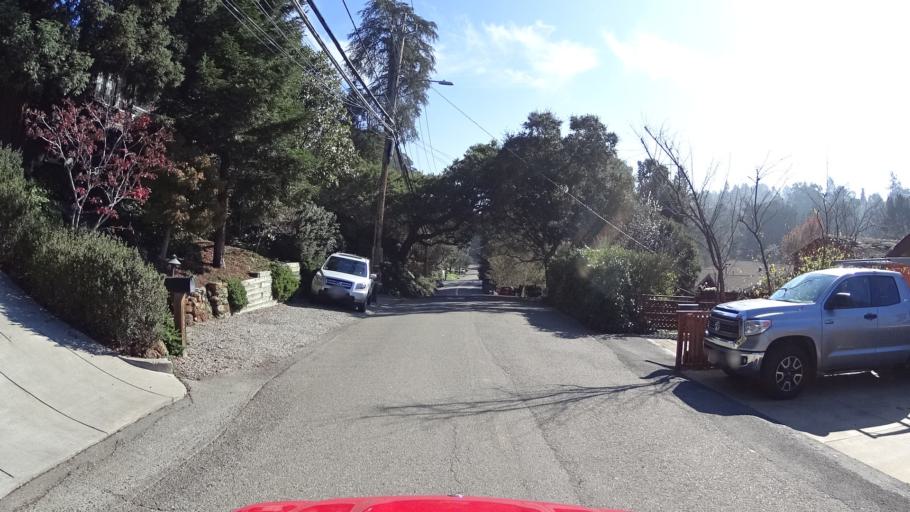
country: US
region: California
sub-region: Alameda County
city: Piedmont
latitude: 37.8372
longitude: -122.2184
